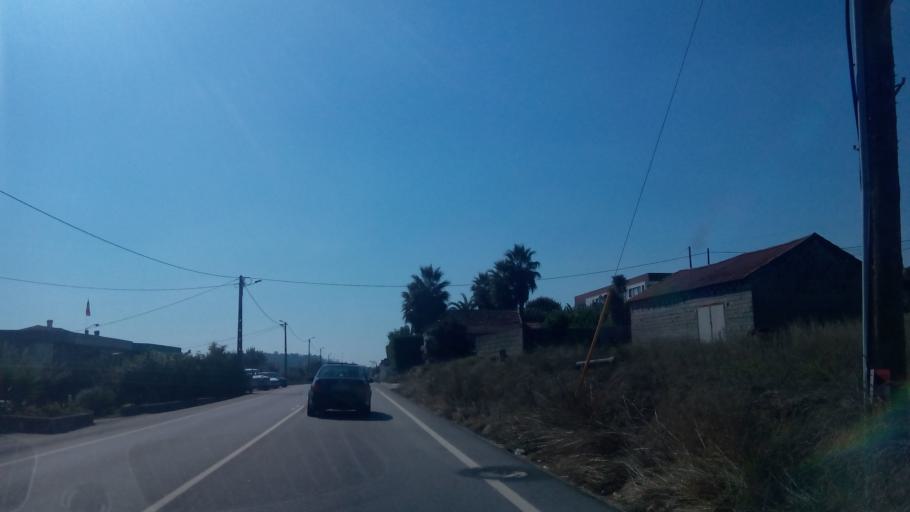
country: PT
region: Porto
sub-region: Lousada
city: Meinedo
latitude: 41.2254
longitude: -8.2355
